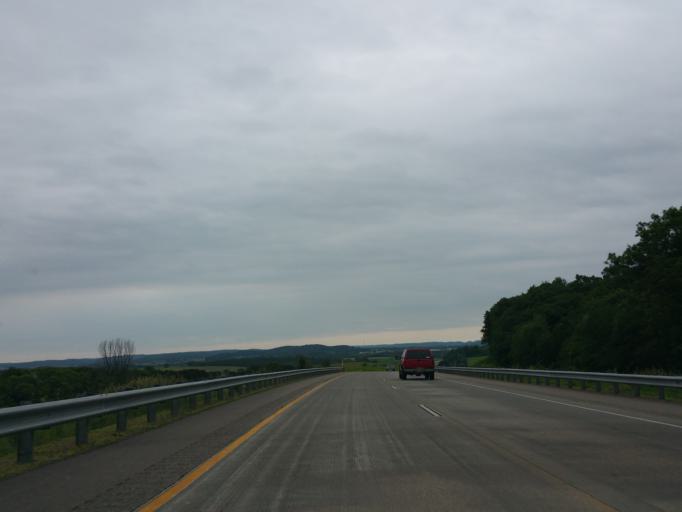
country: US
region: Wisconsin
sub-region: Trempealeau County
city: Osseo
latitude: 44.6083
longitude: -91.2307
